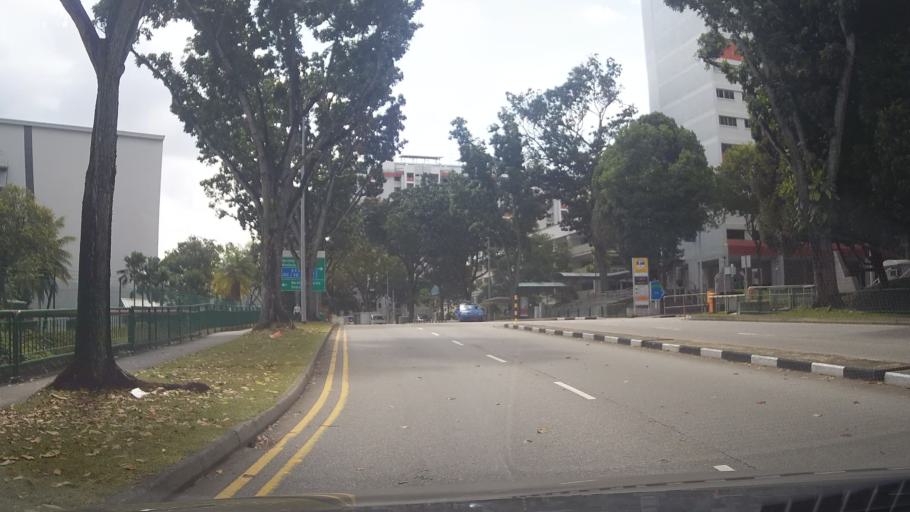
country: MY
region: Johor
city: Johor Bahru
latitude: 1.4429
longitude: 103.7783
